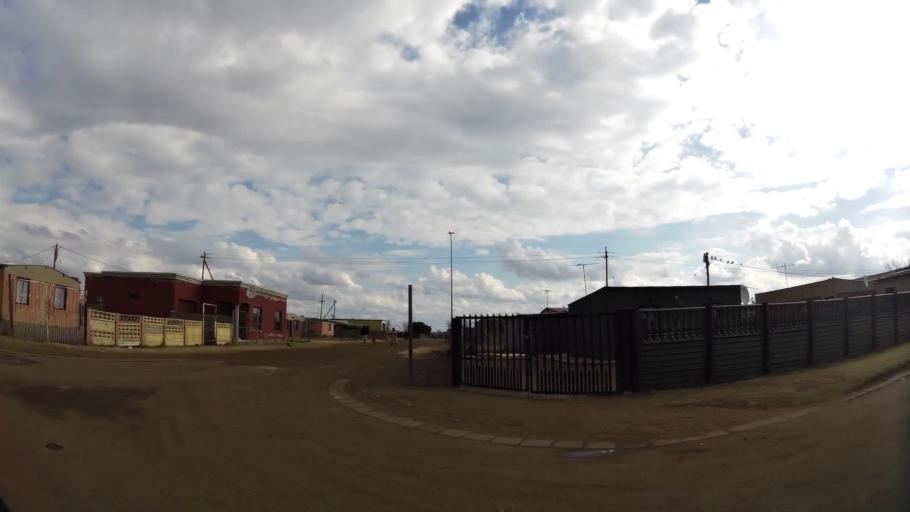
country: ZA
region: Gauteng
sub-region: Sedibeng District Municipality
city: Vanderbijlpark
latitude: -26.6880
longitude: 27.7801
